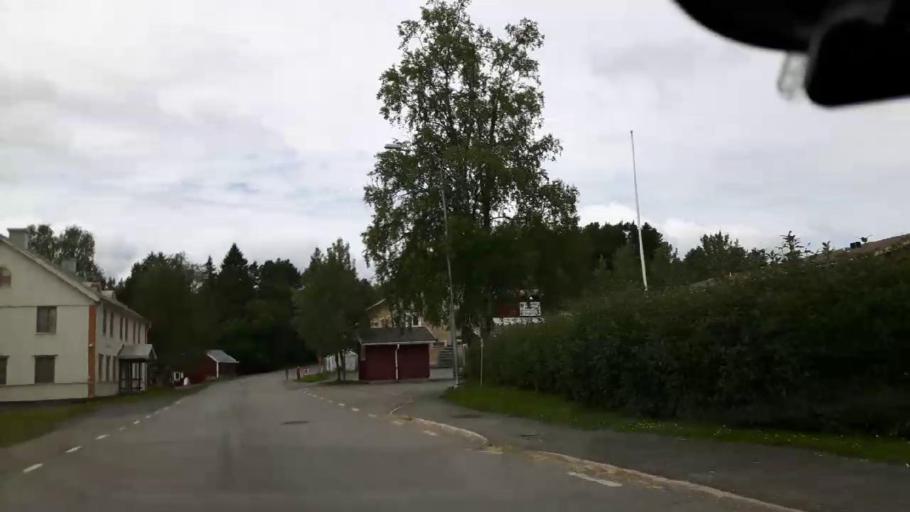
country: SE
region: Jaemtland
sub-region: Krokoms Kommun
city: Valla
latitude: 63.4573
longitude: 14.0657
